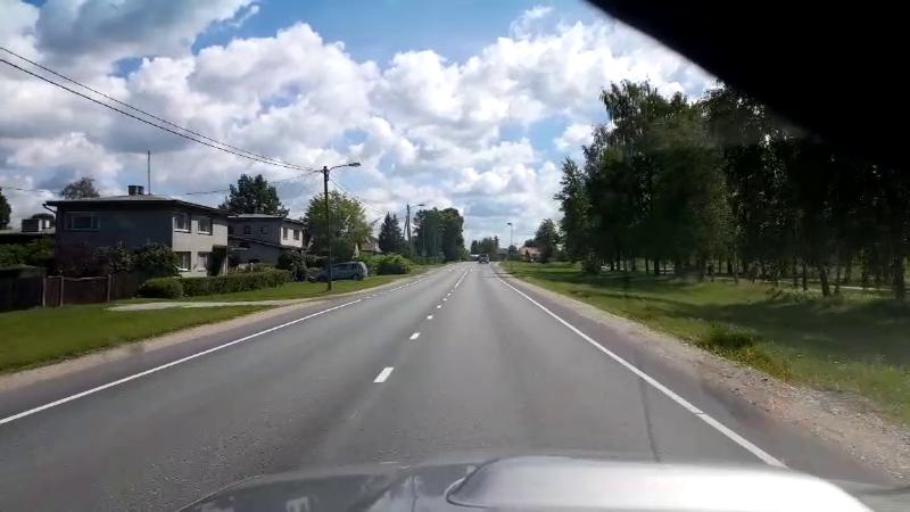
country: EE
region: Laeaene-Virumaa
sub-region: Tapa vald
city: Tapa
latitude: 59.2575
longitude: 25.9550
